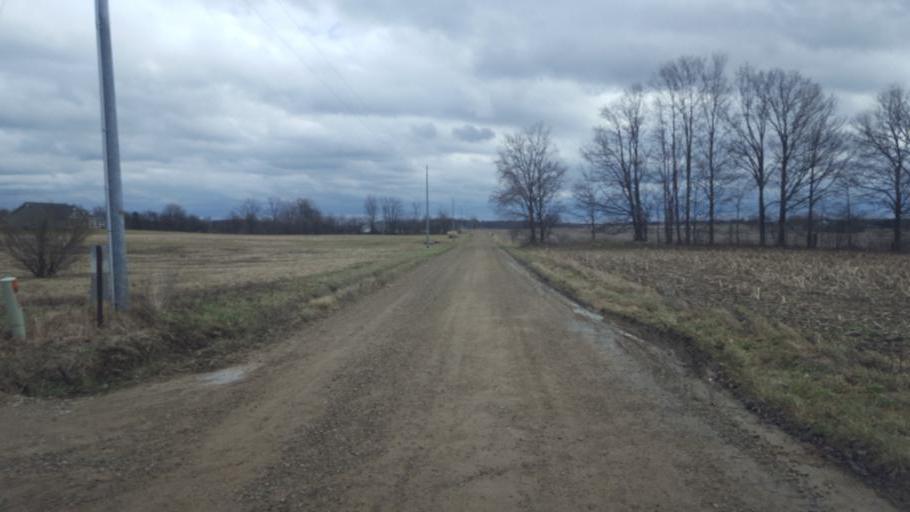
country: US
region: Ohio
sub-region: Knox County
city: Mount Vernon
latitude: 40.3340
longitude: -82.5498
